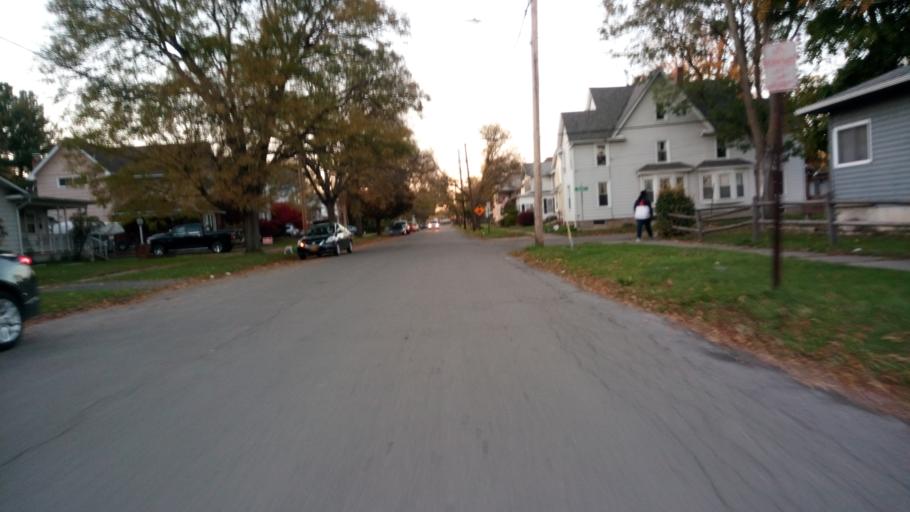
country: US
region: New York
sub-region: Chemung County
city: Elmira
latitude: 42.0814
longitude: -76.8083
